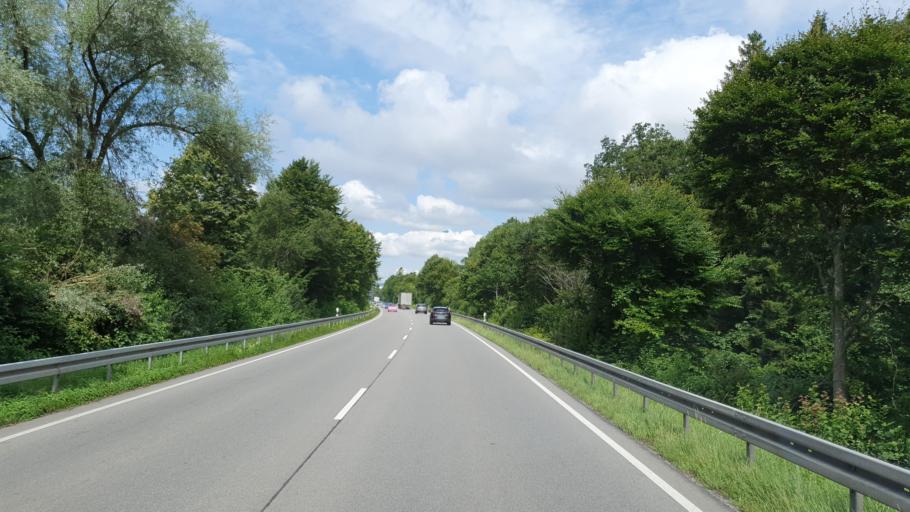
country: DE
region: Baden-Wuerttemberg
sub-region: Tuebingen Region
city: Friedrichshafen
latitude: 47.6496
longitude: 9.5079
